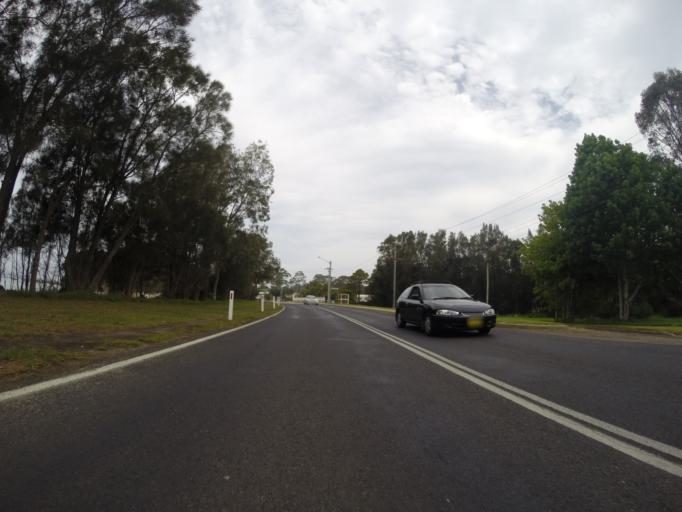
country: AU
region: New South Wales
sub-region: Eurobodalla
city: Batemans Bay
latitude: -35.7371
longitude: 150.2083
